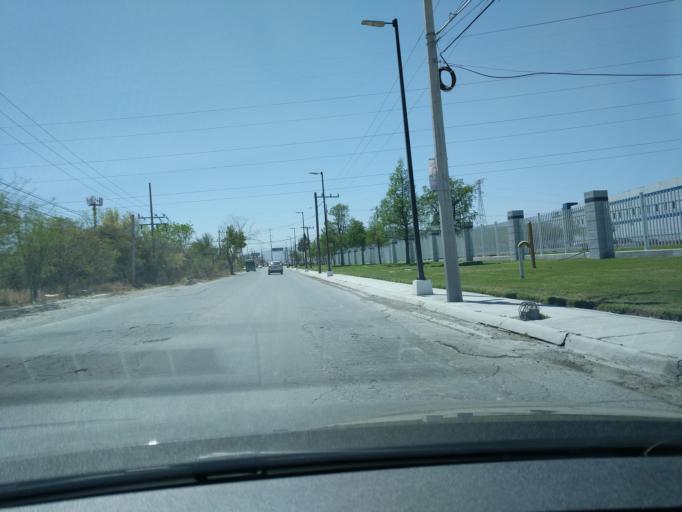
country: MX
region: Nuevo Leon
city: Apodaca
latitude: 25.7886
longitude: -100.1587
